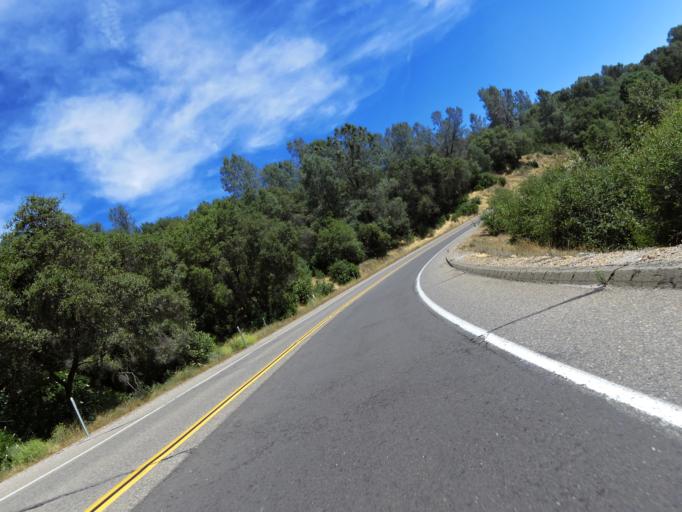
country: US
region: California
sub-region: Mariposa County
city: Mariposa
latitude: 37.5073
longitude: -119.9665
